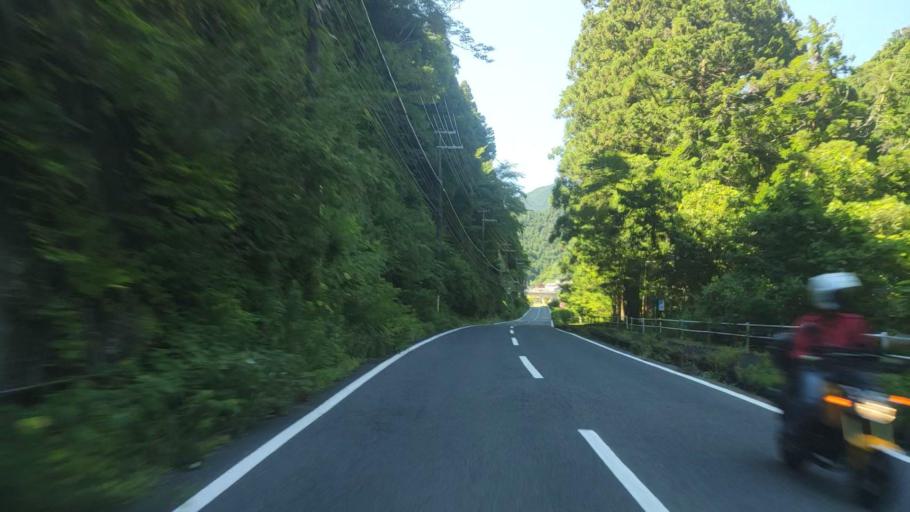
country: JP
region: Nara
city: Yoshino-cho
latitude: 34.2973
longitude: 136.0008
